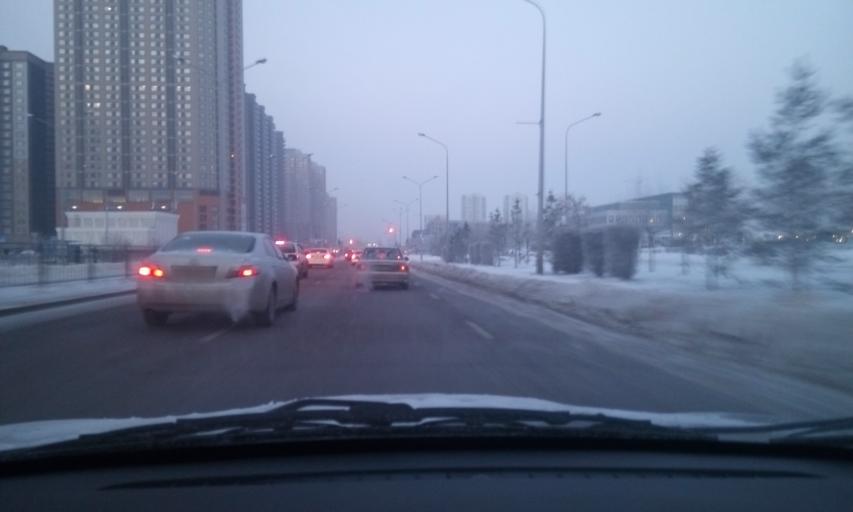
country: KZ
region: Astana Qalasy
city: Astana
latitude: 51.1271
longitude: 71.4735
